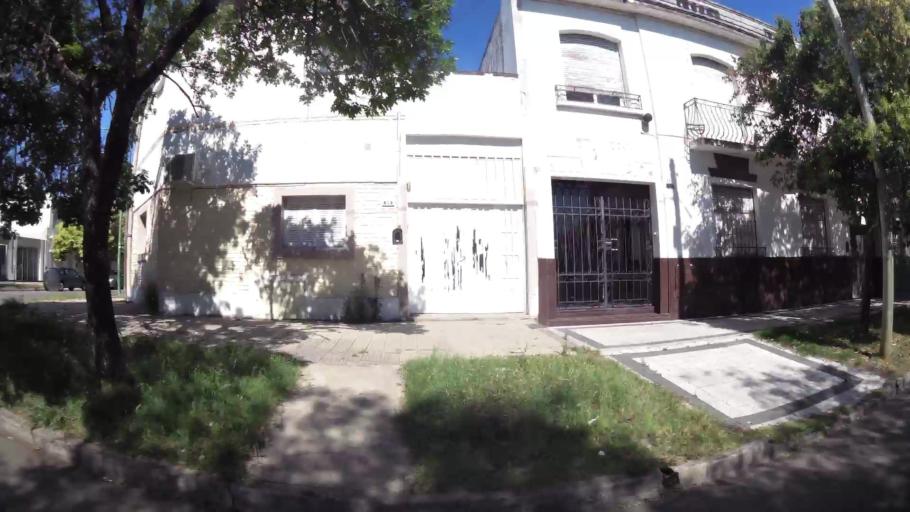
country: AR
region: Cordoba
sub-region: Departamento de Capital
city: Cordoba
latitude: -31.4192
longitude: -64.1683
